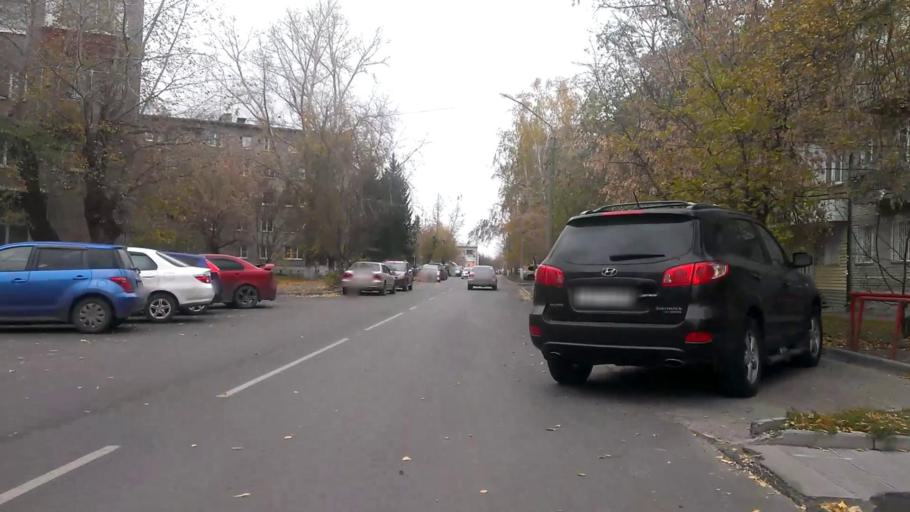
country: RU
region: Altai Krai
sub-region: Gorod Barnaulskiy
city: Barnaul
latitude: 53.3500
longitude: 83.7707
